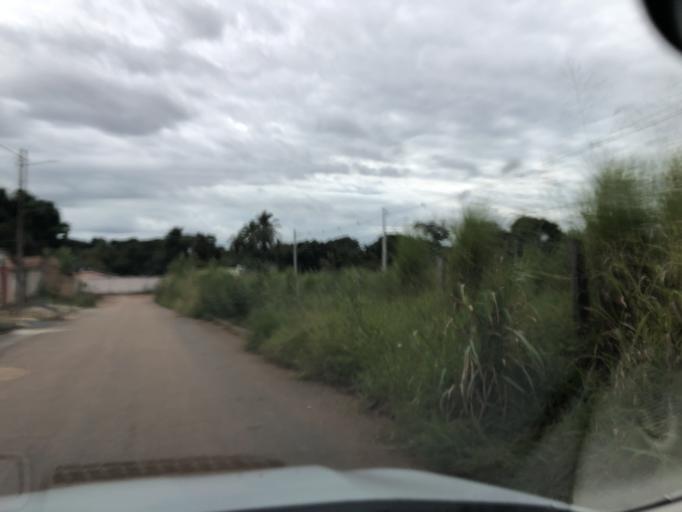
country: BR
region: Goias
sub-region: Luziania
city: Luziania
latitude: -16.1598
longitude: -47.9502
